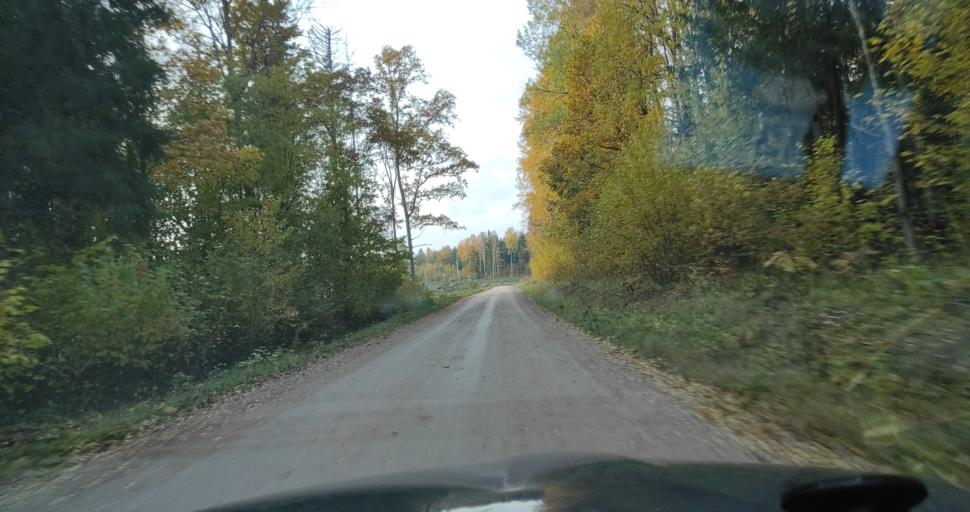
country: LV
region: Vainode
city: Vainode
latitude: 56.6316
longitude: 21.8165
